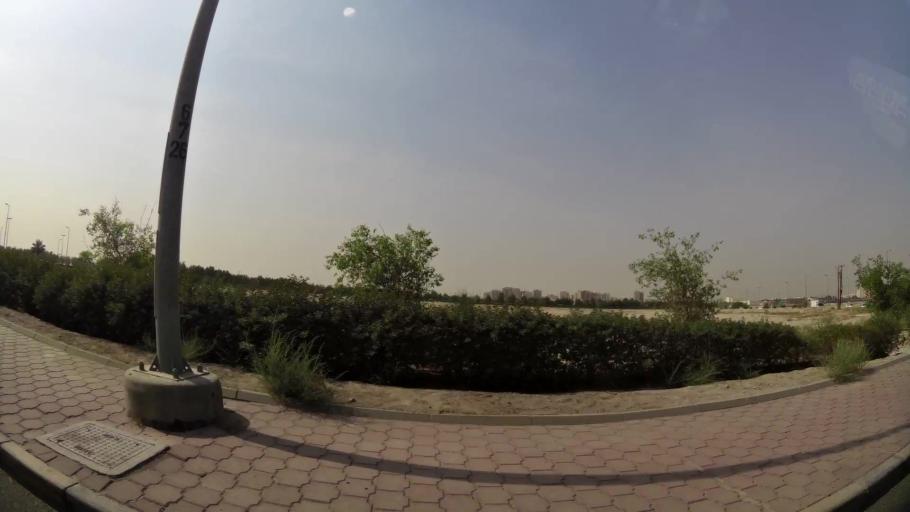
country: KW
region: Al Farwaniyah
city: Al Farwaniyah
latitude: 29.2591
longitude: 47.9571
